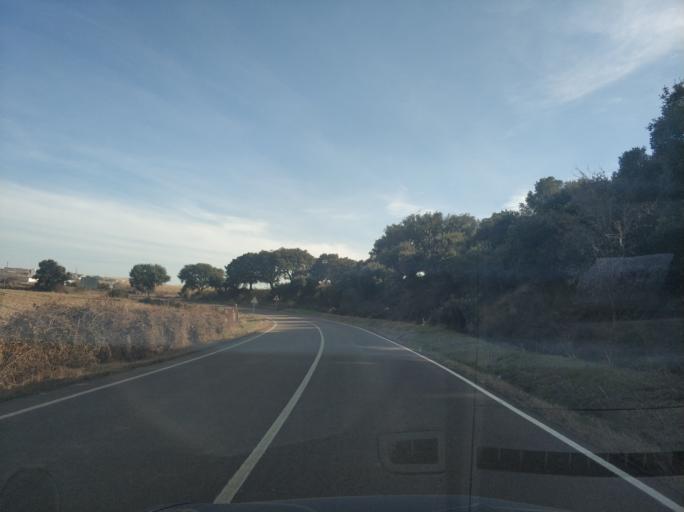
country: ES
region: Castille and Leon
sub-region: Provincia de Salamanca
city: Doninos de Salamanca
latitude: 40.9898
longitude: -5.7316
